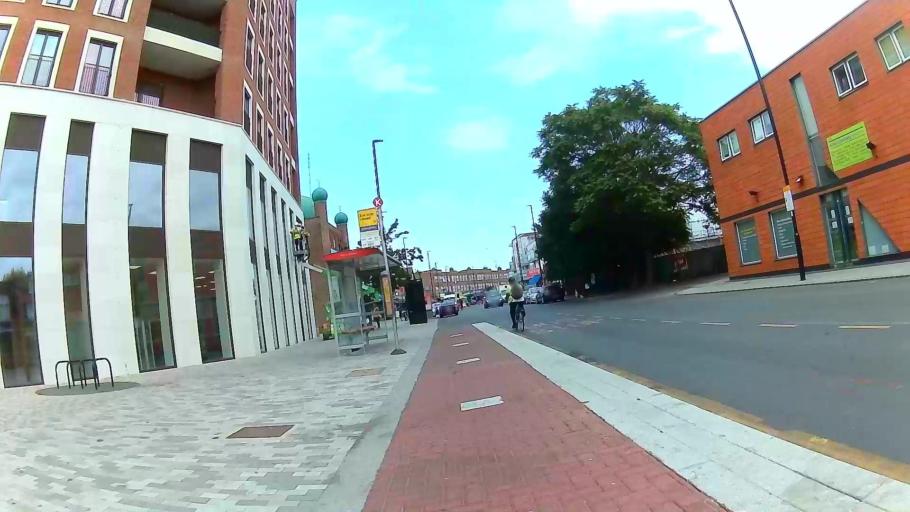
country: GB
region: England
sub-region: Greater London
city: Enfield
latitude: 51.6455
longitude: -0.0465
